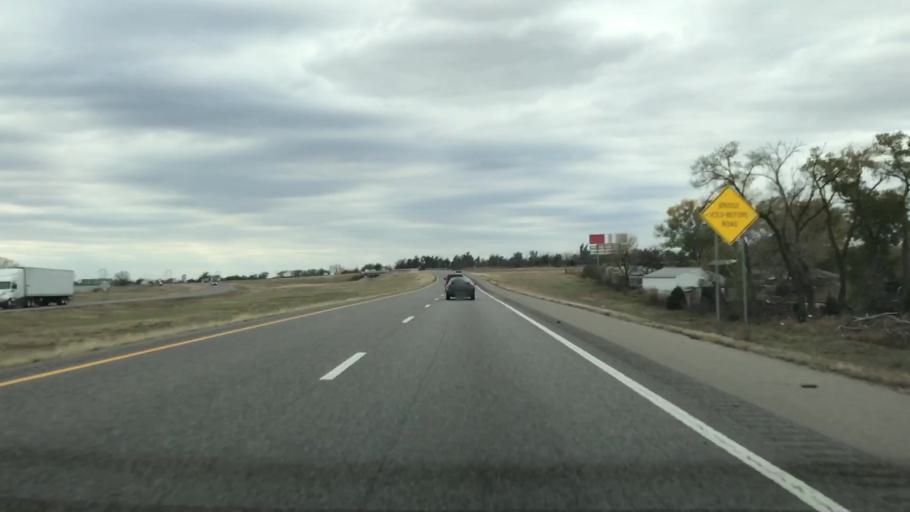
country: US
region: Oklahoma
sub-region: Beckham County
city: Elk City
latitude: 35.3858
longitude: -99.5069
